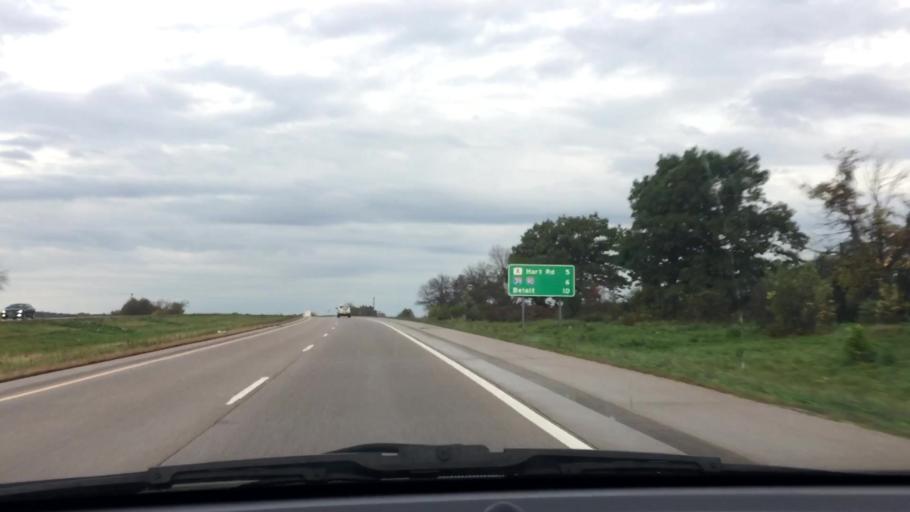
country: US
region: Wisconsin
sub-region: Rock County
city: Clinton
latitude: 42.5734
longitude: -88.8846
